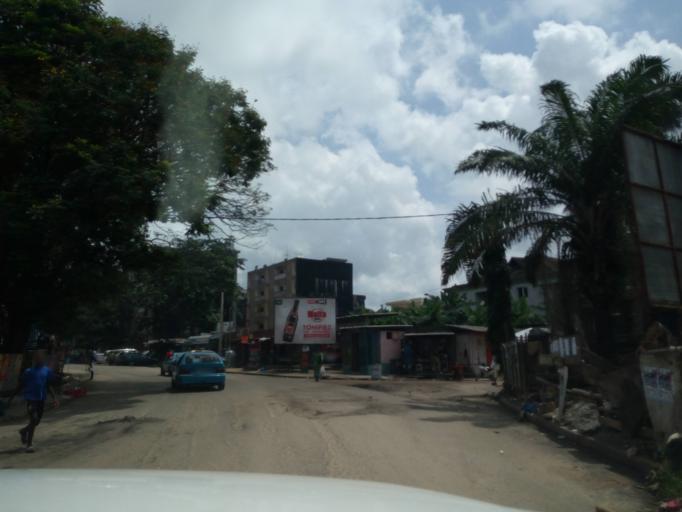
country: CI
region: Lagunes
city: Abidjan
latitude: 5.3409
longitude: -4.0984
